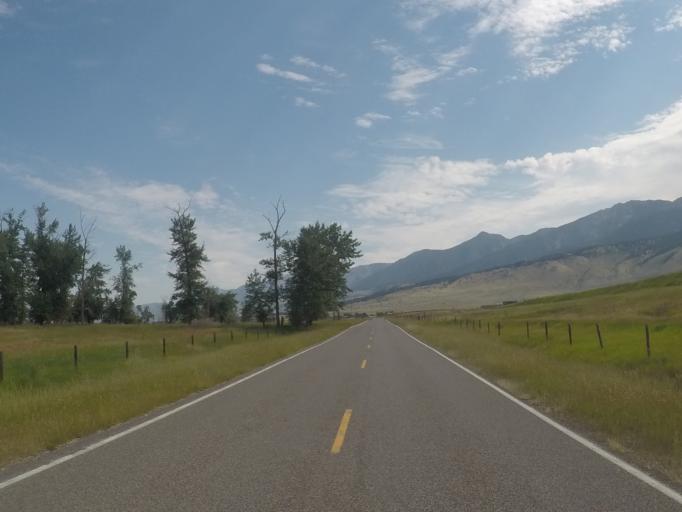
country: US
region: Montana
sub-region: Park County
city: Livingston
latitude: 45.4225
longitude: -110.6274
